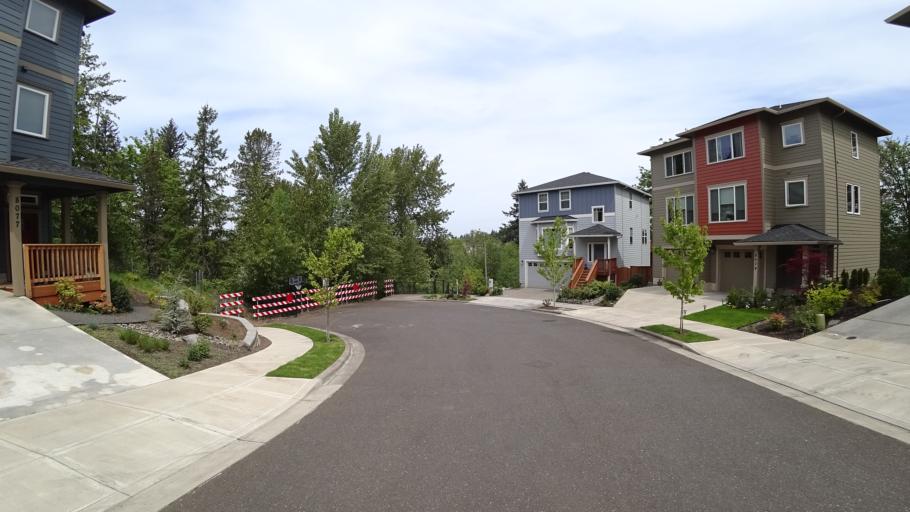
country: US
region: Oregon
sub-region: Washington County
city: Aloha
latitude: 45.4612
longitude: -122.8542
